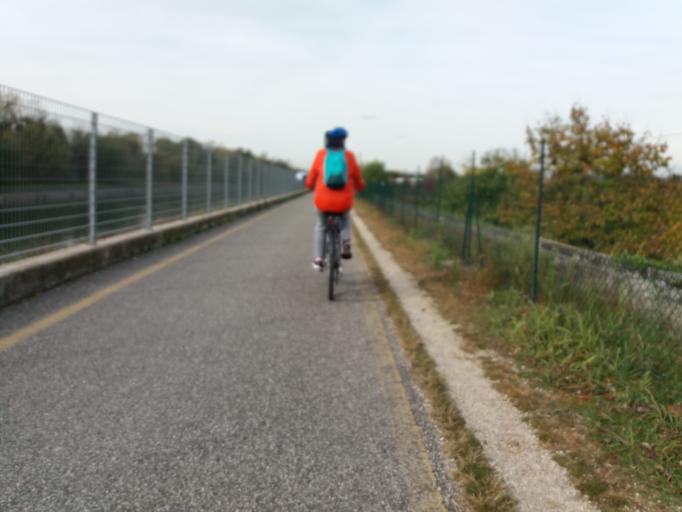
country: IT
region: Veneto
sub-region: Provincia di Verona
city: San Vito al Mantico
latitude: 45.4708
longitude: 10.8867
